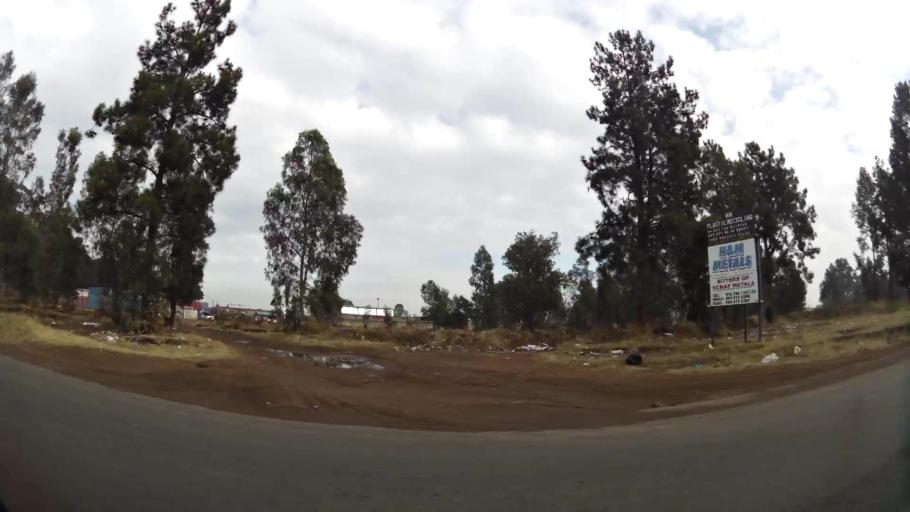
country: ZA
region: Gauteng
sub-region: Sedibeng District Municipality
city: Vanderbijlpark
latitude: -26.6941
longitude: 27.8113
